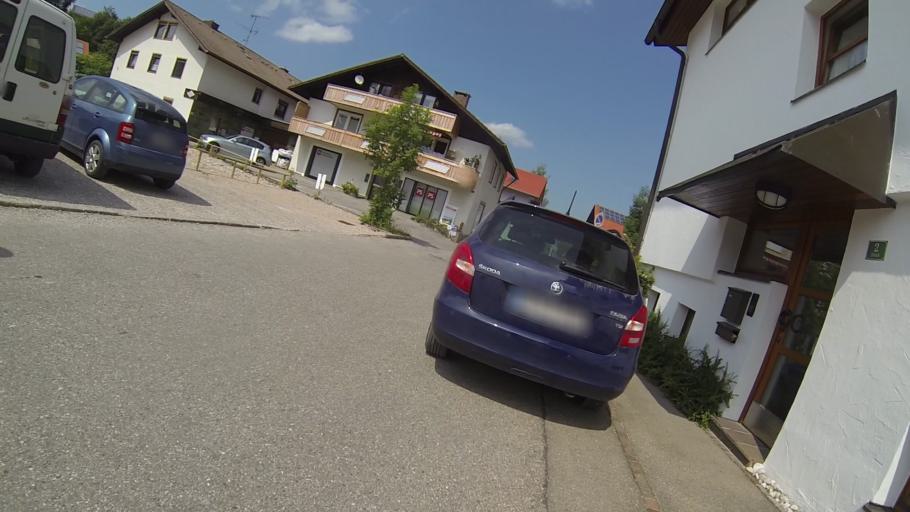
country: DE
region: Bavaria
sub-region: Swabia
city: Nesselwang
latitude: 47.6227
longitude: 10.4992
